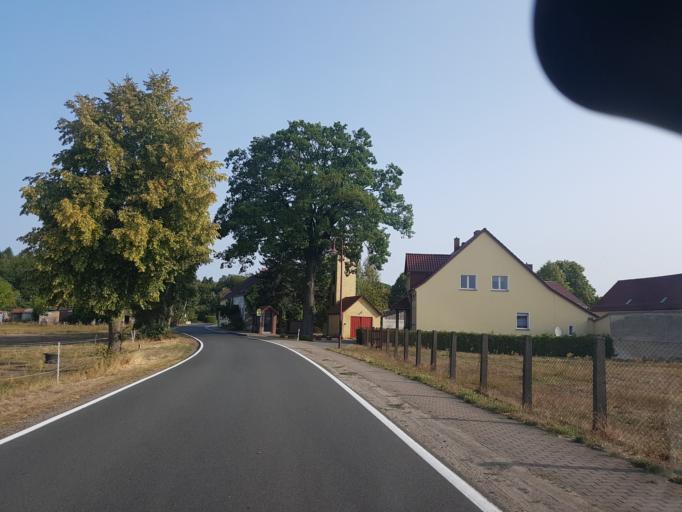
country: DE
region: Brandenburg
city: Wiesenburg
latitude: 52.0691
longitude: 12.3845
